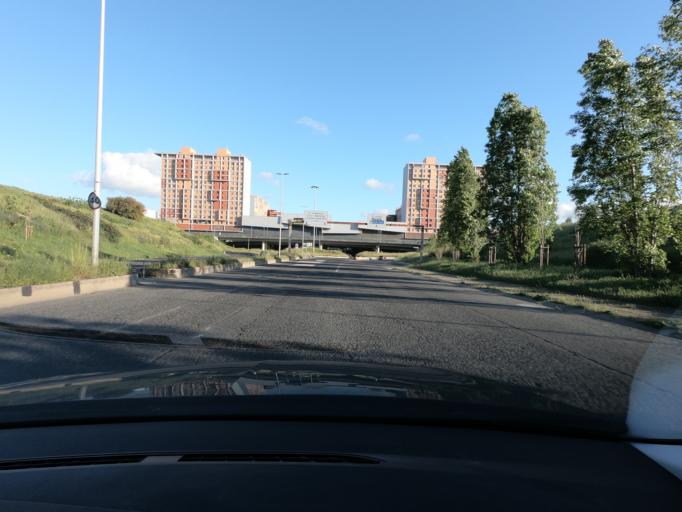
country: PT
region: Lisbon
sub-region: Loures
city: Moscavide
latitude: 38.7521
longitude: -9.1186
